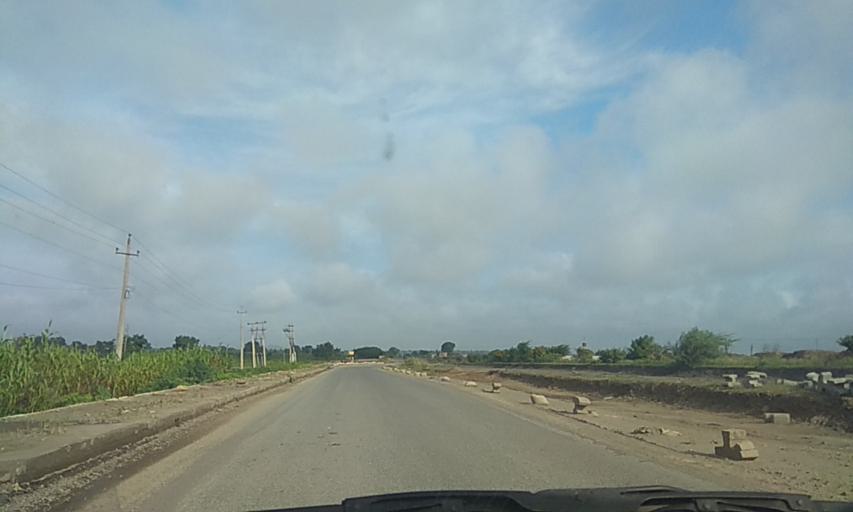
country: IN
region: Karnataka
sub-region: Haveri
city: Haveri
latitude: 14.8555
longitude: 75.3271
